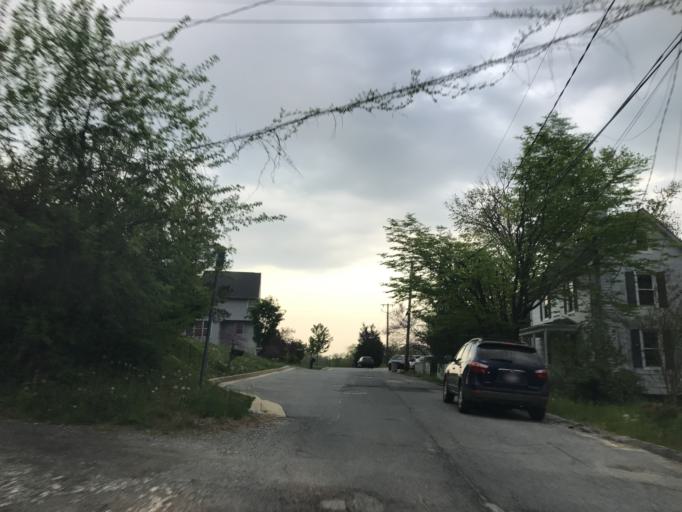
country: US
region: Maryland
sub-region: Baltimore County
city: Overlea
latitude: 39.3667
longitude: -76.5133
